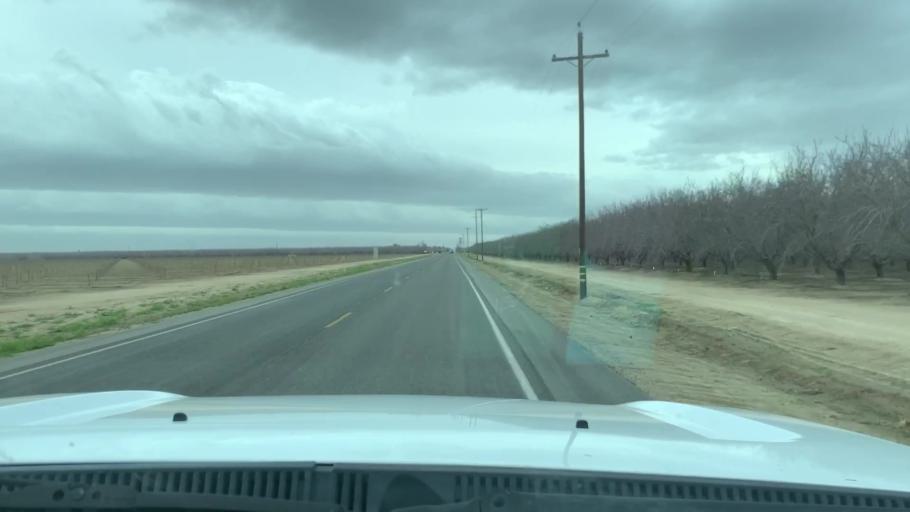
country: US
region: California
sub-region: Kern County
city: Wasco
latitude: 35.5581
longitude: -119.3067
